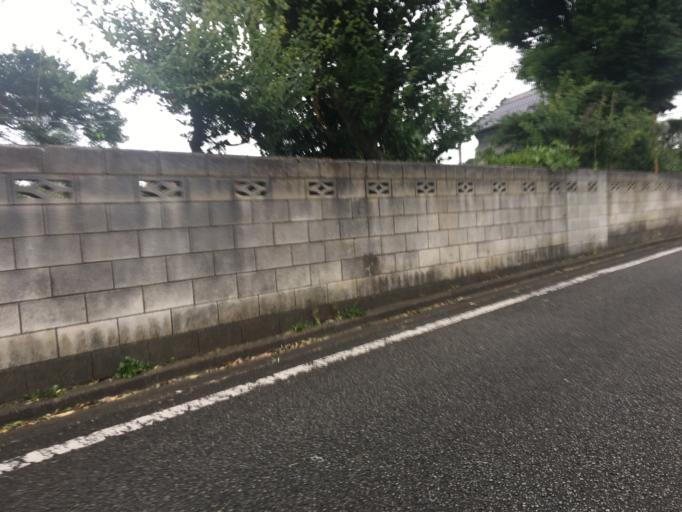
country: JP
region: Tokyo
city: Higashimurayama-shi
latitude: 35.7644
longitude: 139.4624
